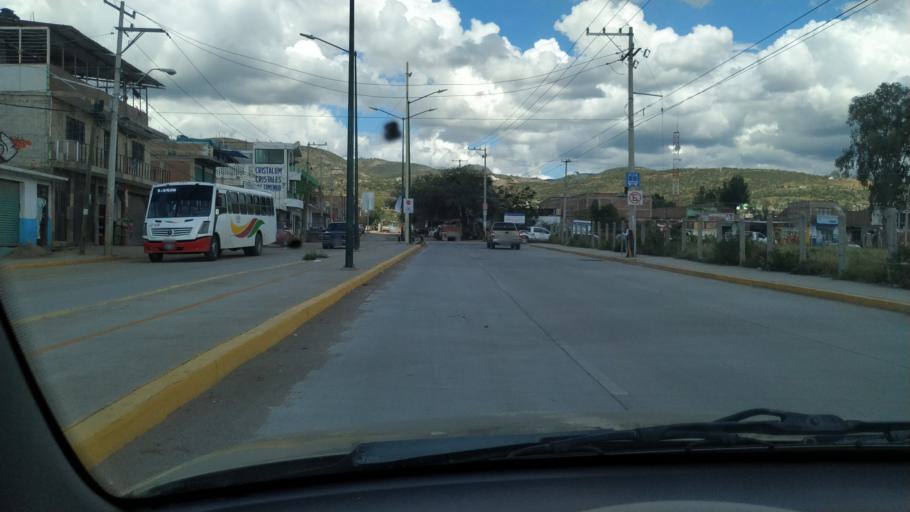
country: MX
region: Guanajuato
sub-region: Leon
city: Medina
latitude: 21.1516
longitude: -101.6275
